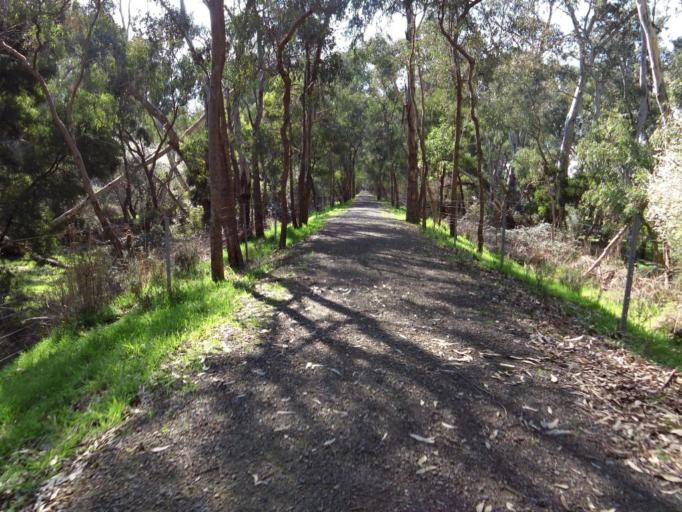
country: AU
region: Victoria
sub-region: Murrindindi
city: Alexandra
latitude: -37.1588
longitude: 145.5675
